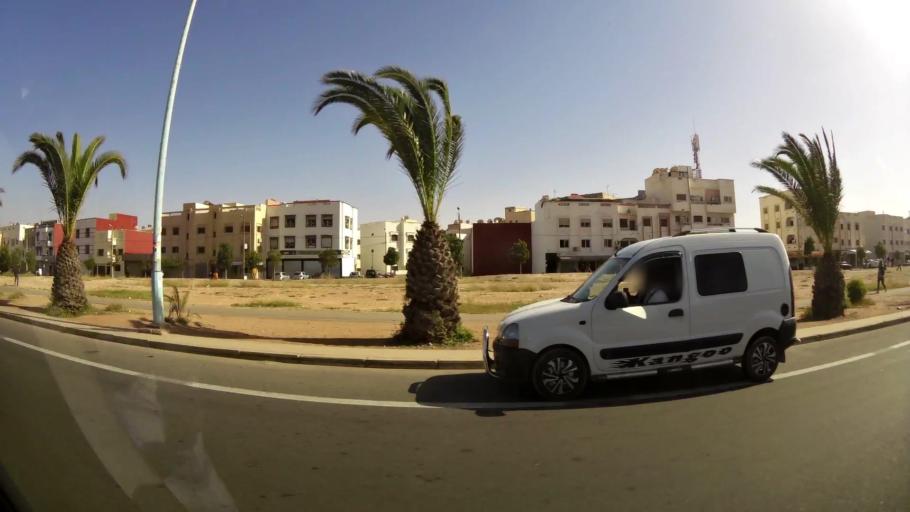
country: MA
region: Oued ed Dahab-Lagouira
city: Dakhla
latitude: 30.4041
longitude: -9.5481
